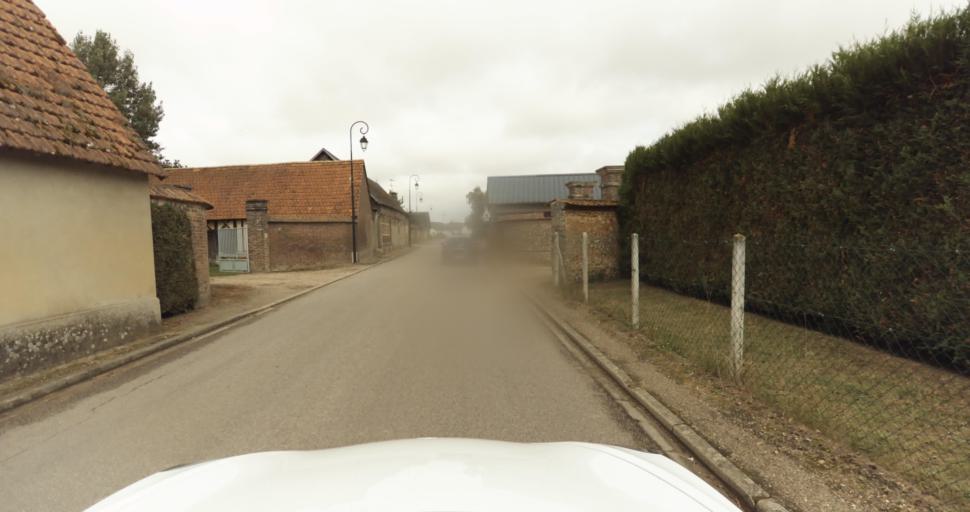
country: FR
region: Haute-Normandie
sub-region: Departement de l'Eure
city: Aviron
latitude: 49.0484
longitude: 1.0863
